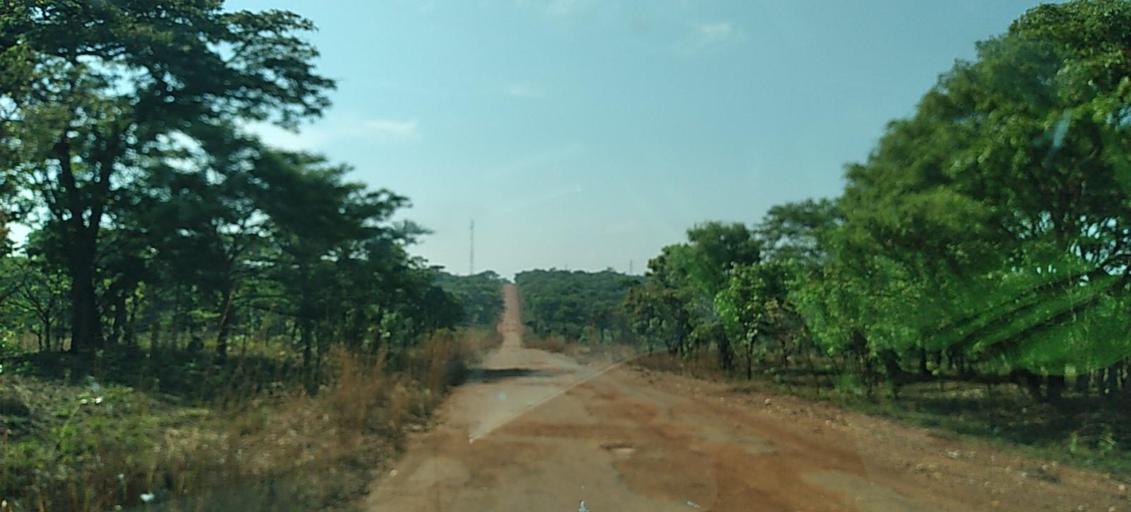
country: ZM
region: North-Western
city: Mwinilunga
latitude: -11.8053
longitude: 25.0797
